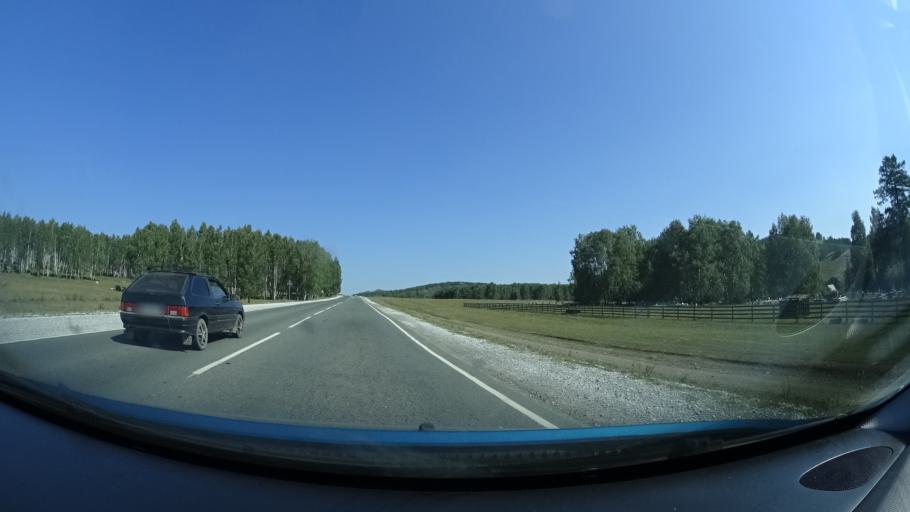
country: RU
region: Bashkortostan
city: Abzakovo
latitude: 53.8393
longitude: 58.5808
